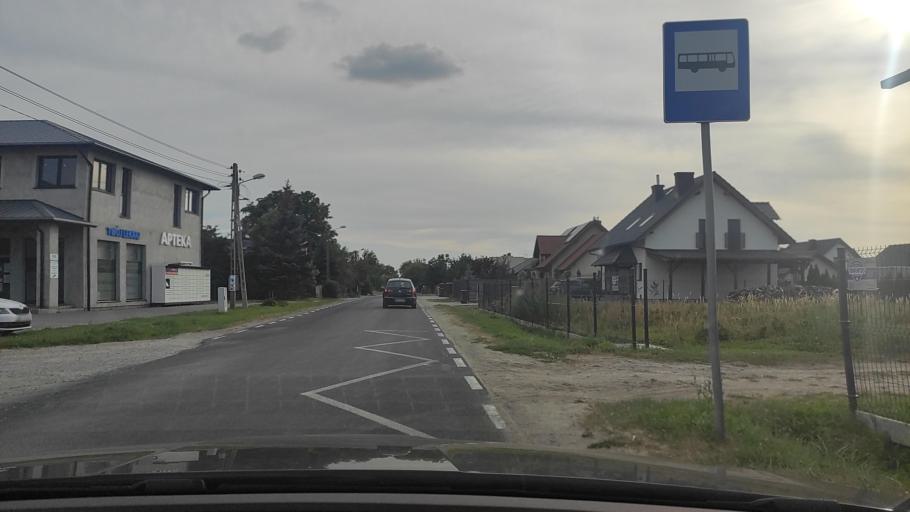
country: PL
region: Greater Poland Voivodeship
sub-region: Powiat poznanski
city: Kleszczewo
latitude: 52.3669
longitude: 17.1421
